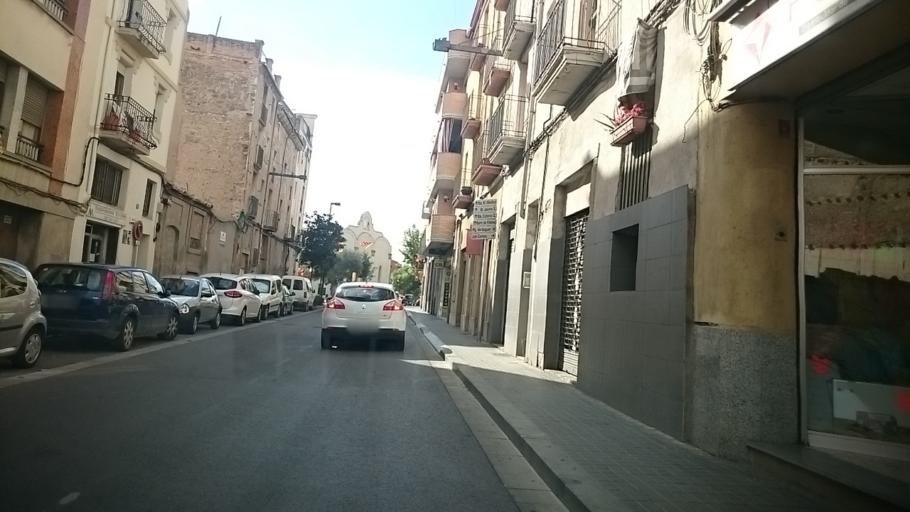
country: ES
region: Catalonia
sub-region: Provincia de Barcelona
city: Igualada
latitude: 41.5804
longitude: 1.6116
